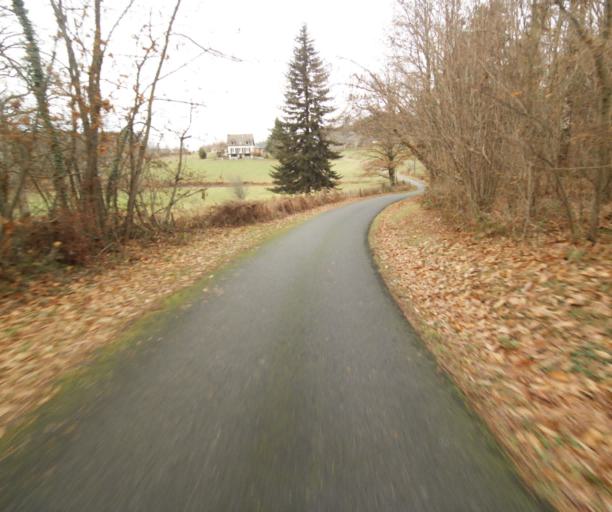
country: FR
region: Limousin
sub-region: Departement de la Correze
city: Chameyrat
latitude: 45.2457
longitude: 1.6752
